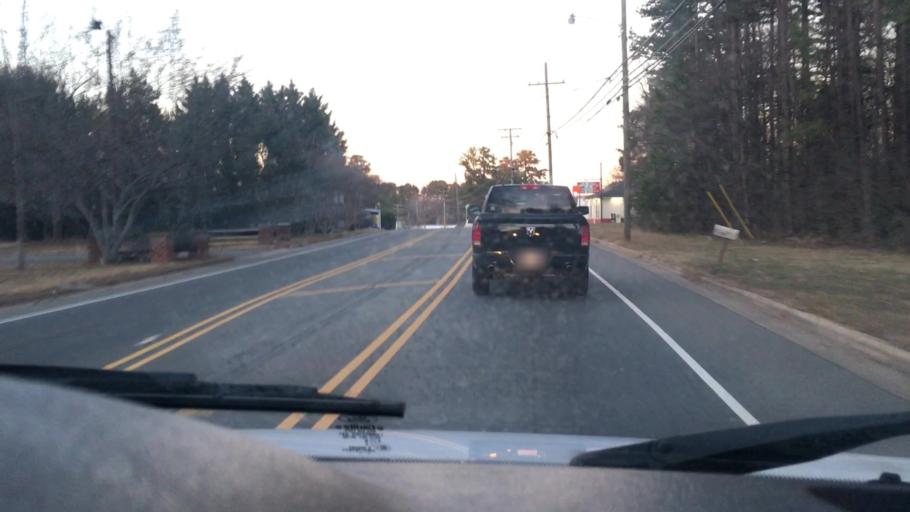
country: US
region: North Carolina
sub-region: Mecklenburg County
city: Huntersville
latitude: 35.4181
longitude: -80.8420
